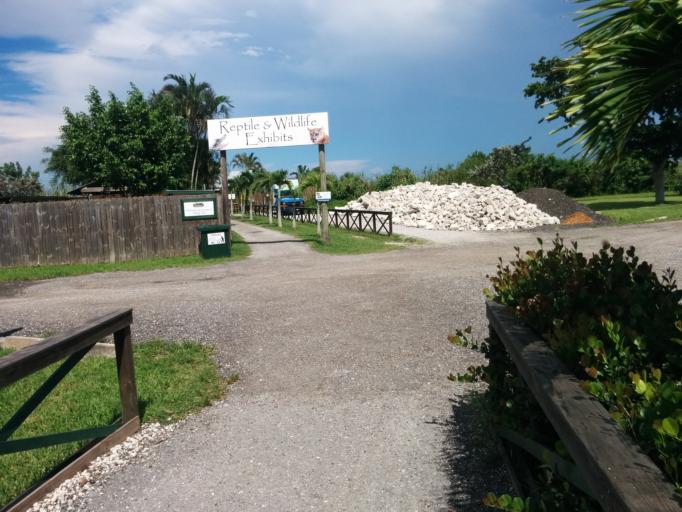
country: US
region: Florida
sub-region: Broward County
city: Weston
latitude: 26.1770
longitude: -80.4472
